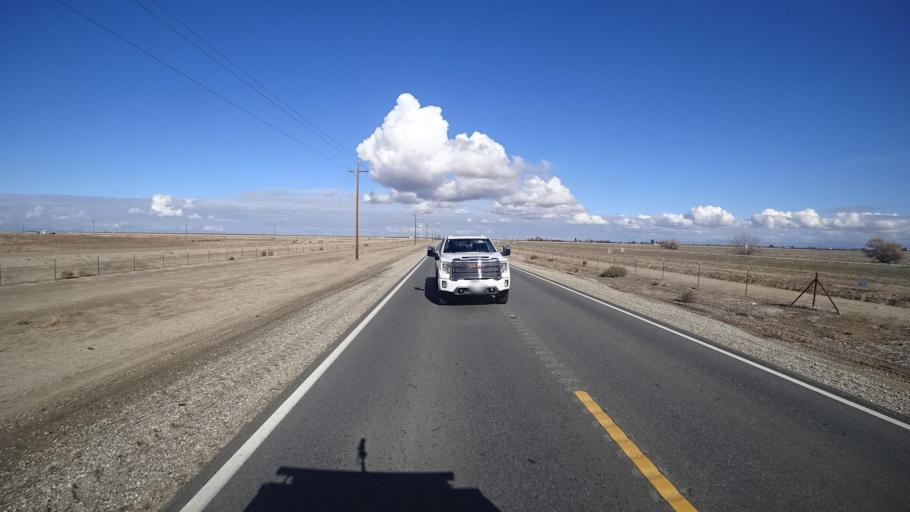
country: US
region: California
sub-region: Kern County
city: Rosedale
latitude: 35.3420
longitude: -119.2523
